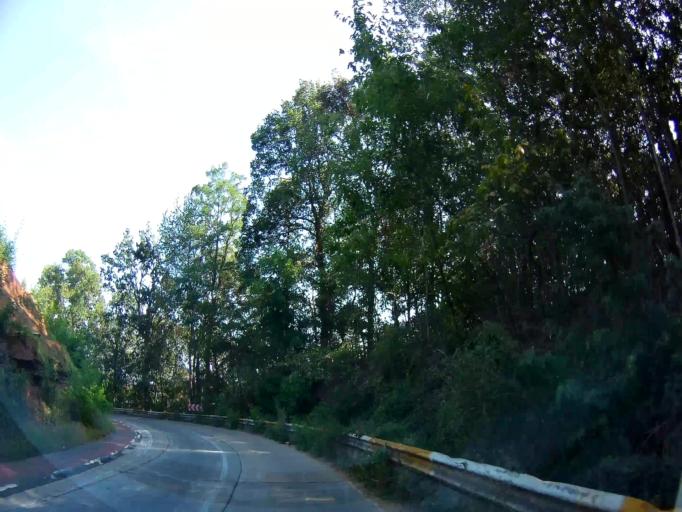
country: BE
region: Flanders
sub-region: Provincie Vlaams-Brabant
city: Diest
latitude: 50.9942
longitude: 5.0325
